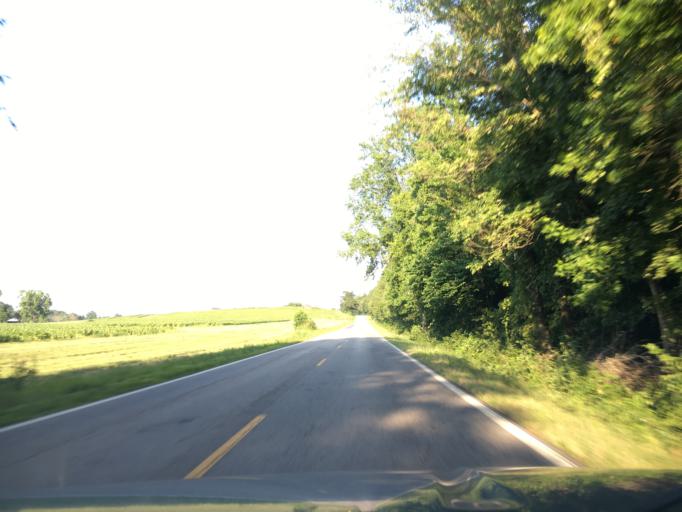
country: US
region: Virginia
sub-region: Pittsylvania County
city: Chatham
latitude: 36.8280
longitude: -79.2984
